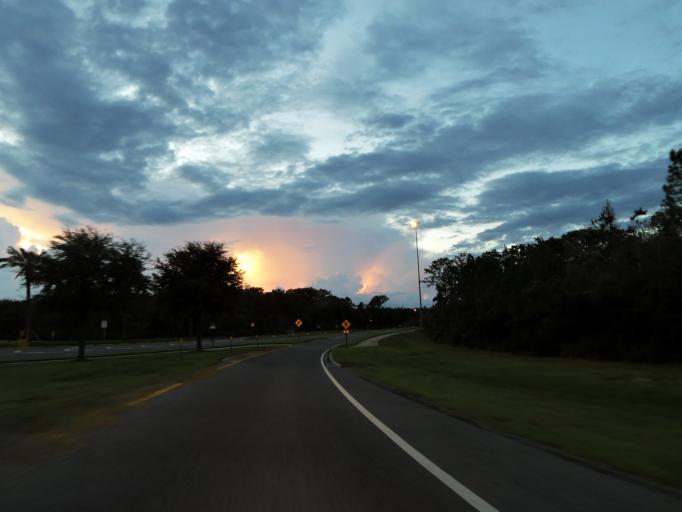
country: US
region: Florida
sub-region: Saint Johns County
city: Palm Valley
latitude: 30.1122
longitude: -81.4471
